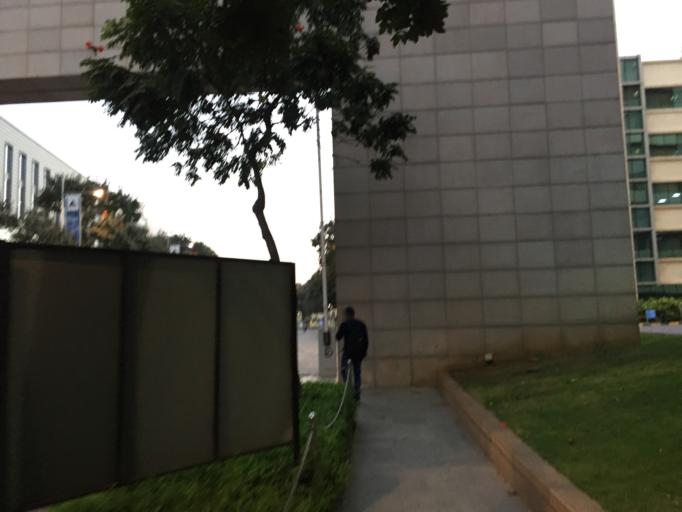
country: IN
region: Karnataka
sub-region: Bangalore Urban
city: Yelahanka
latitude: 13.0456
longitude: 77.6206
